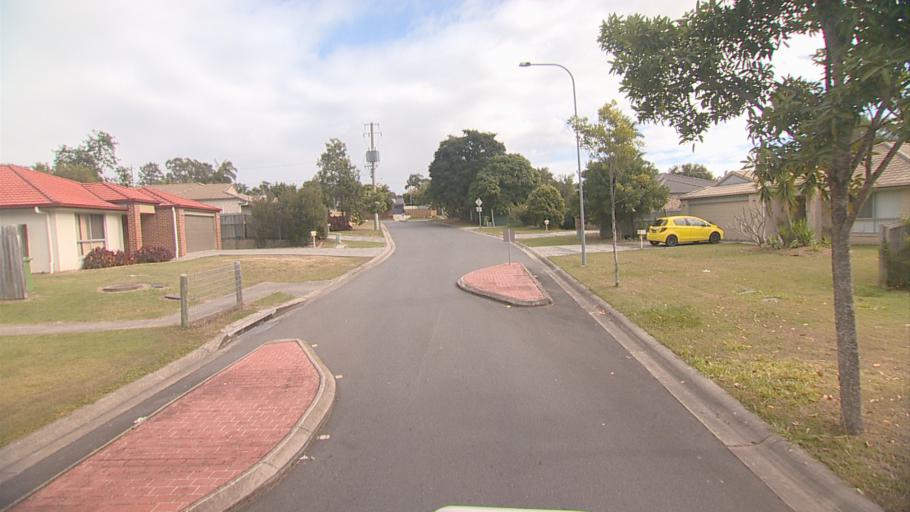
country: AU
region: Queensland
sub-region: Logan
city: Woodridge
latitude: -27.6665
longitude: 153.0587
